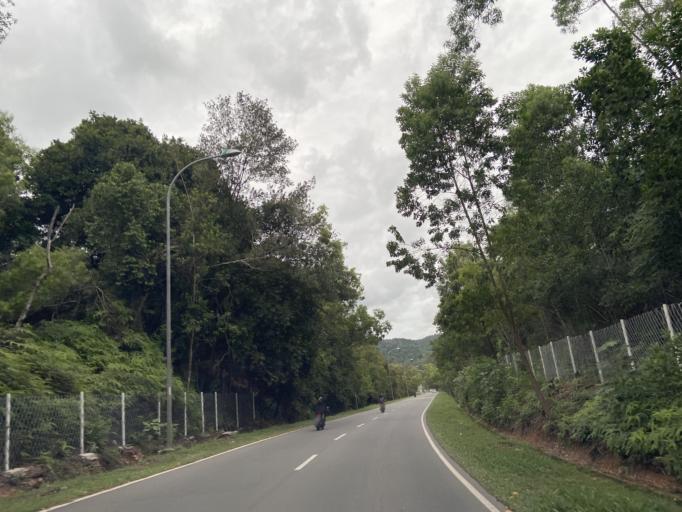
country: SG
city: Singapore
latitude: 1.1147
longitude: 104.0155
